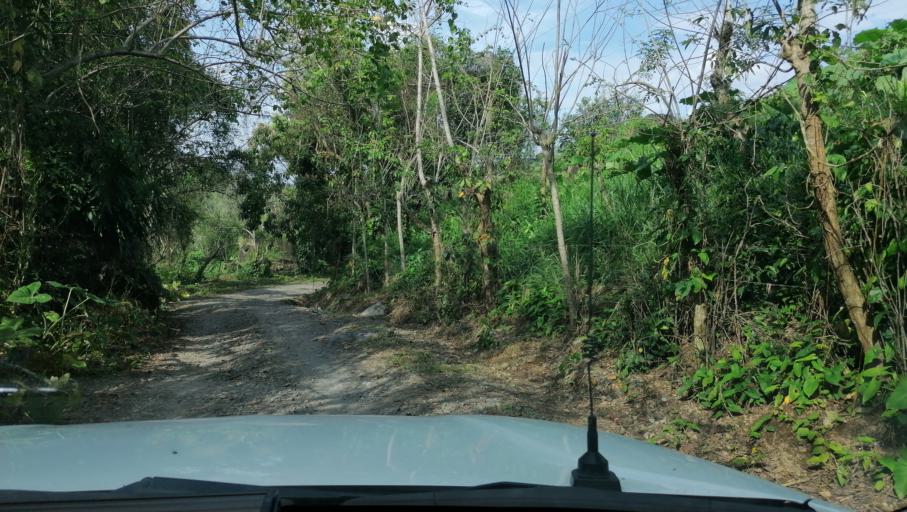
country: MX
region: Chiapas
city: Ostuacan
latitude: 17.4566
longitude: -93.2422
